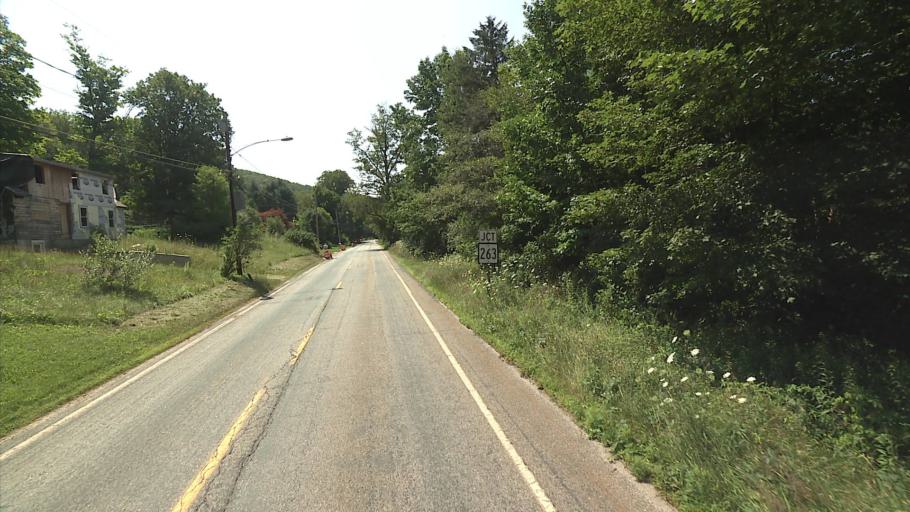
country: US
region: Connecticut
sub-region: Litchfield County
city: Winchester Center
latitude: 41.9015
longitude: -73.1764
